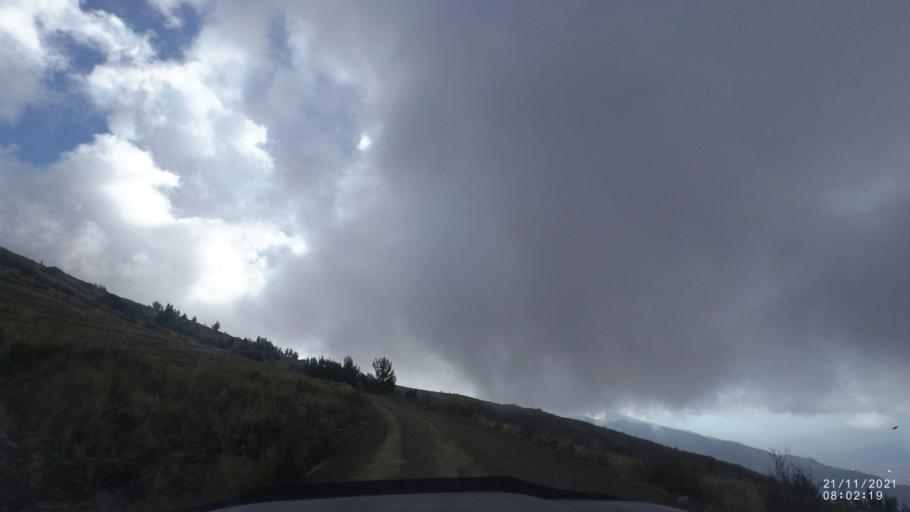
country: BO
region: Cochabamba
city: Cochabamba
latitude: -17.2891
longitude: -66.2166
